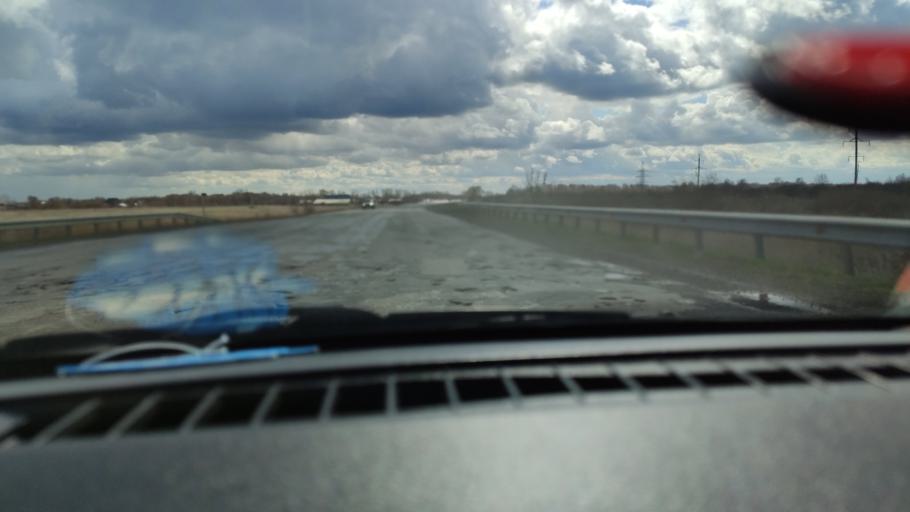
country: RU
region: Samara
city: Tol'yatti
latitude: 53.6645
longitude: 49.4213
